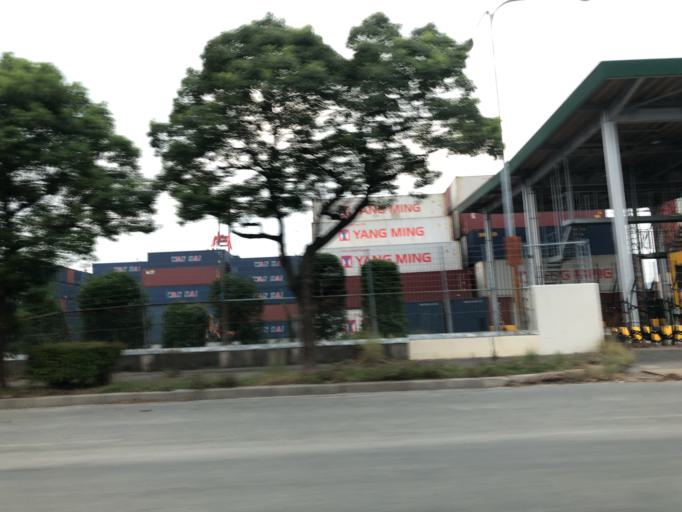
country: JP
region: Hyogo
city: Ashiya
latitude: 34.6828
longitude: 135.2579
